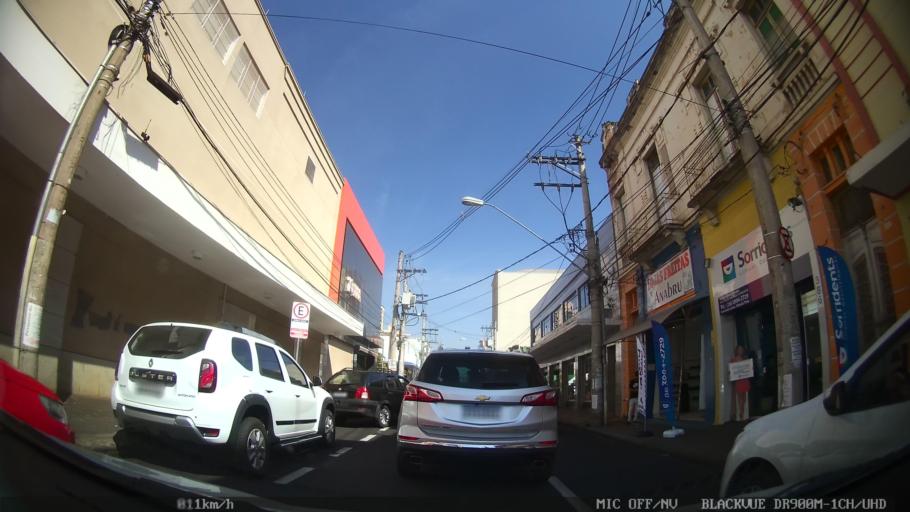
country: BR
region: Sao Paulo
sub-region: Ribeirao Preto
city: Ribeirao Preto
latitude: -21.1734
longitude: -47.8110
